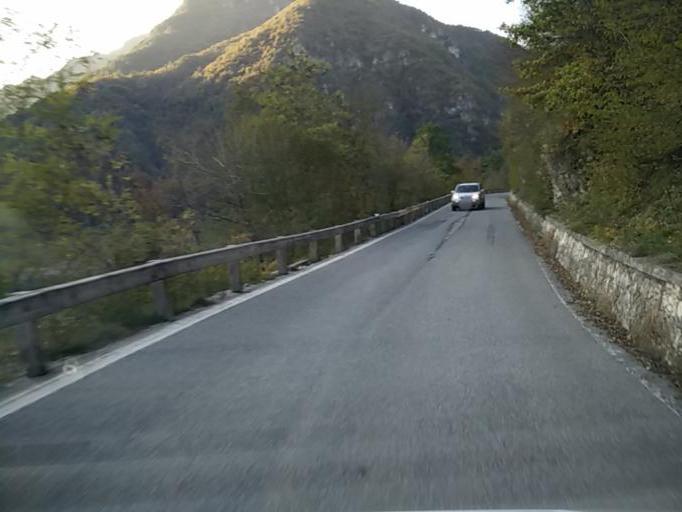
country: IT
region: Lombardy
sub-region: Provincia di Brescia
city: Gargnano
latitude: 45.7114
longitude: 10.6131
